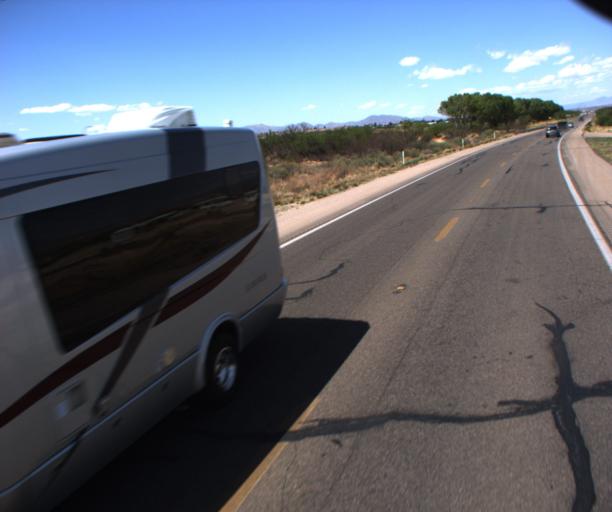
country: US
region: Arizona
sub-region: Cochise County
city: Benson
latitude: 31.9365
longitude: -110.2858
